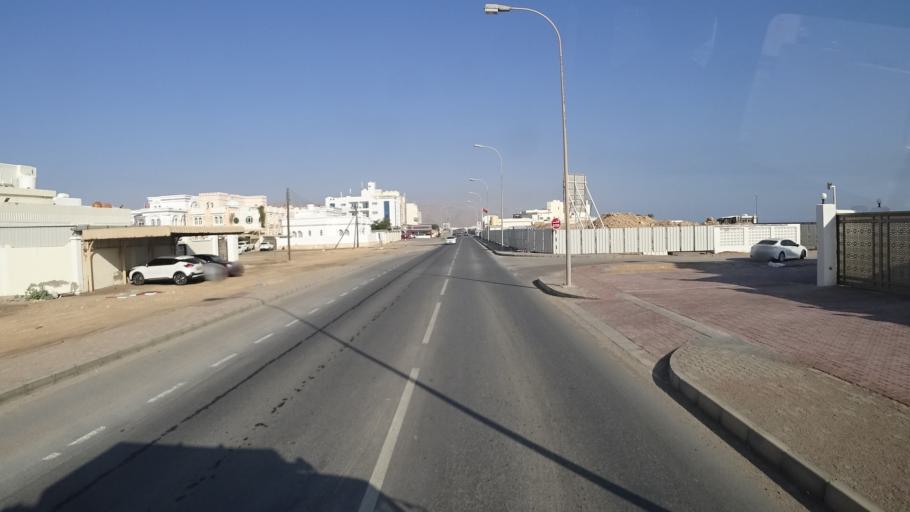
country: OM
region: Ash Sharqiyah
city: Sur
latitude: 22.5941
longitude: 59.4957
